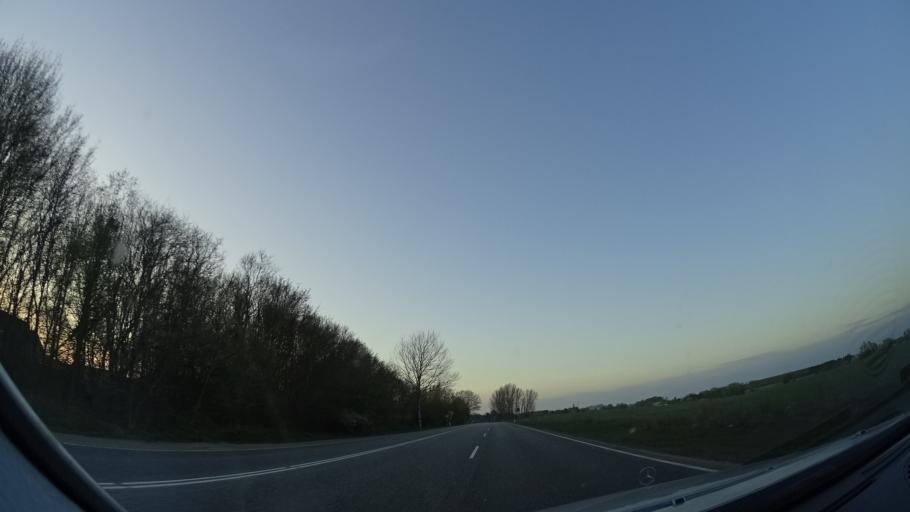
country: DK
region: Zealand
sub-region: Roskilde Kommune
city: Roskilde
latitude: 55.6054
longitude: 12.1009
